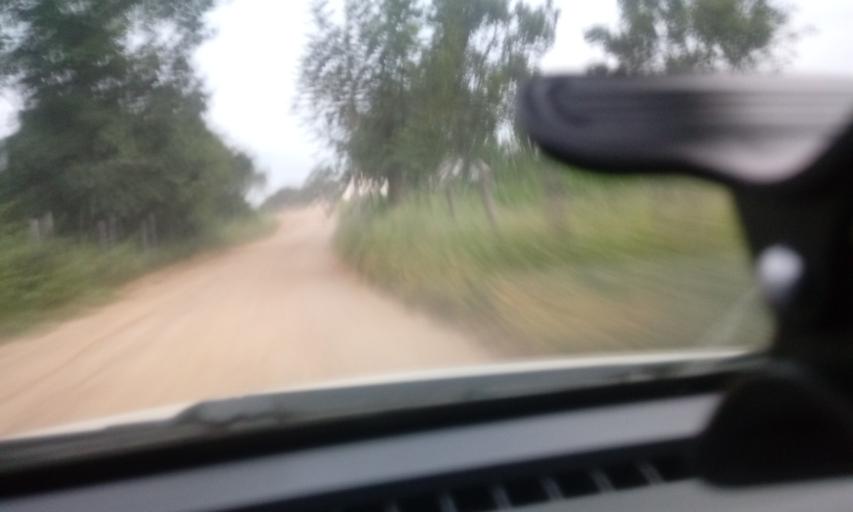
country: BR
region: Bahia
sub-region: Riacho De Santana
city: Riacho de Santana
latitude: -13.8199
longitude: -42.7635
